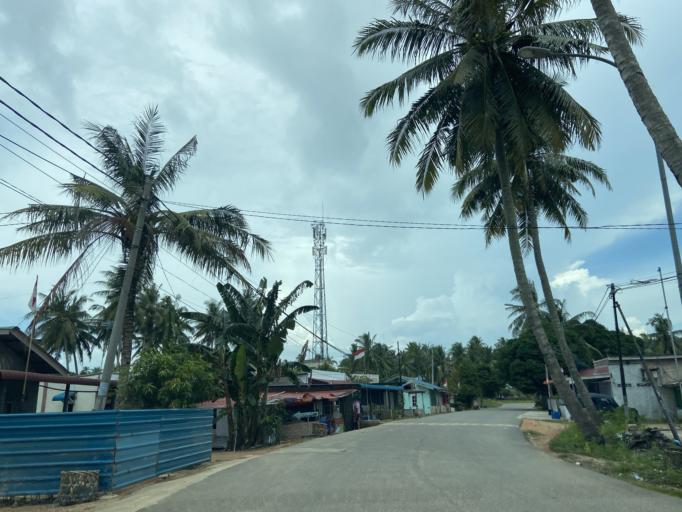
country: SG
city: Singapore
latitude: 1.1531
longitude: 104.1380
